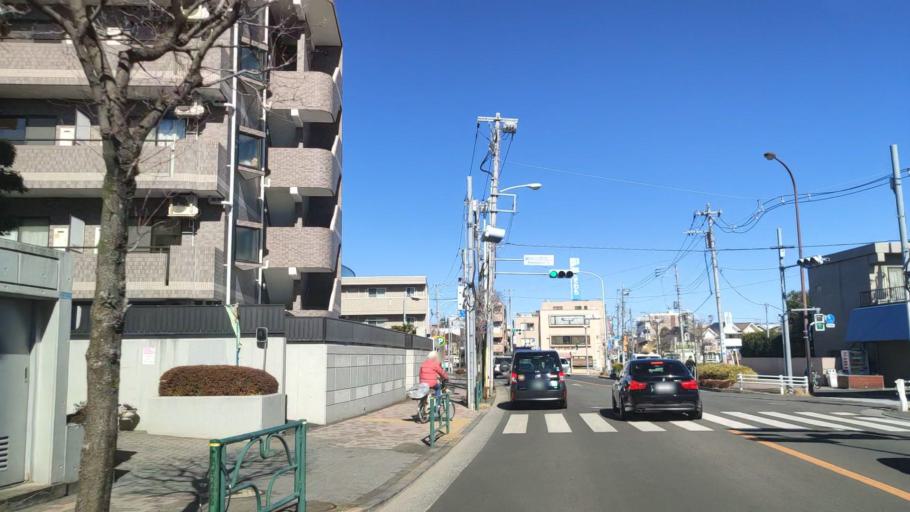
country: JP
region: Tokyo
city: Mitaka-shi
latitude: 35.6761
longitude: 139.5676
